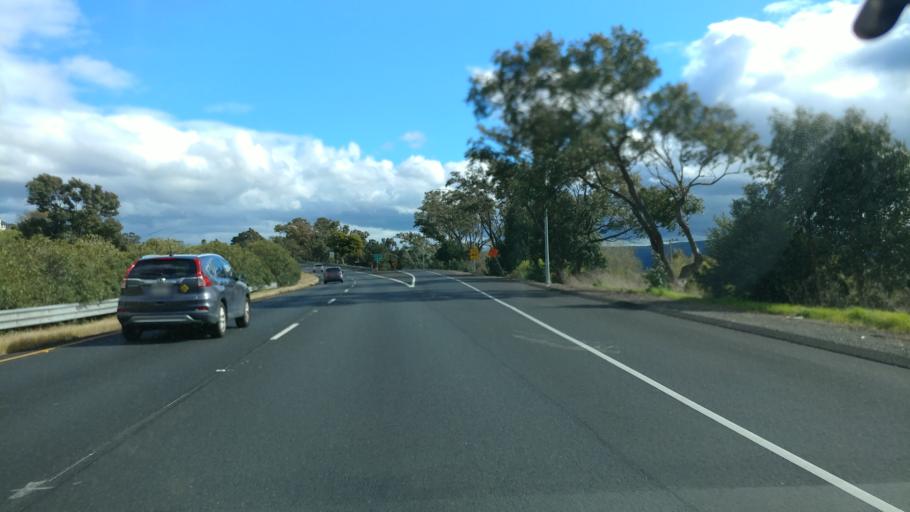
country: US
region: California
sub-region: Contra Costa County
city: Crockett
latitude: 38.0709
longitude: -122.1853
